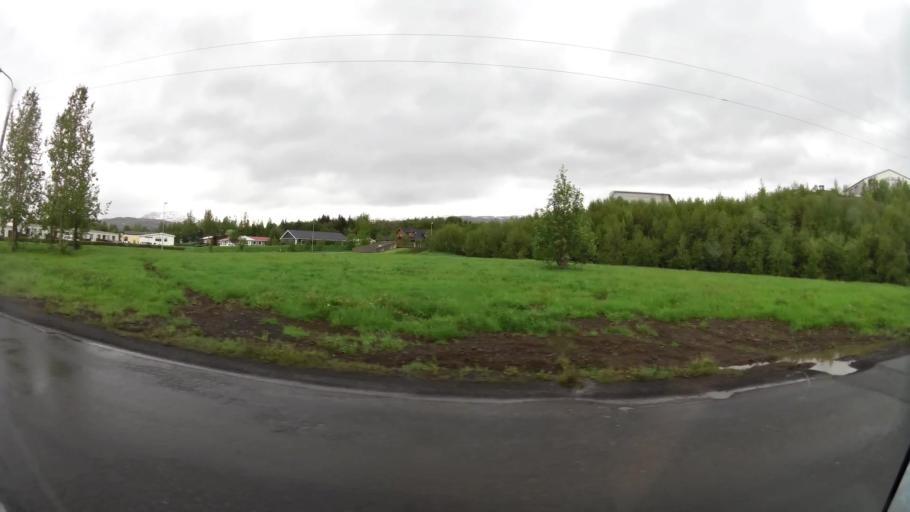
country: IS
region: Northeast
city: Akureyri
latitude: 65.6973
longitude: -18.1158
